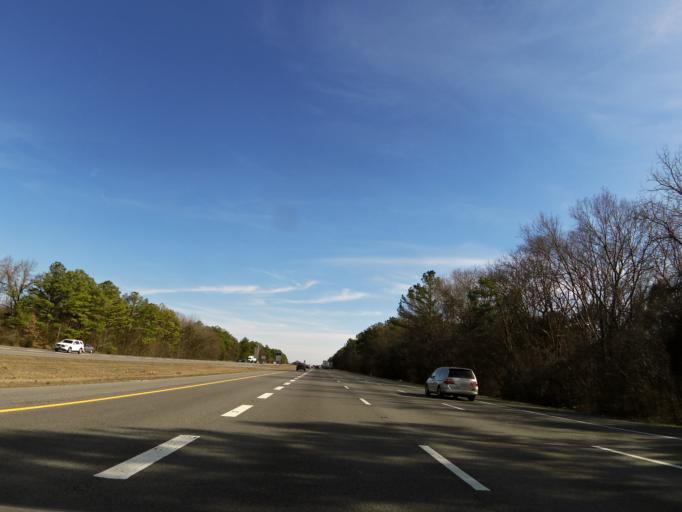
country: US
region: Tennessee
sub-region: Rutherford County
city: Smyrna
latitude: 35.9077
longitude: -86.5021
